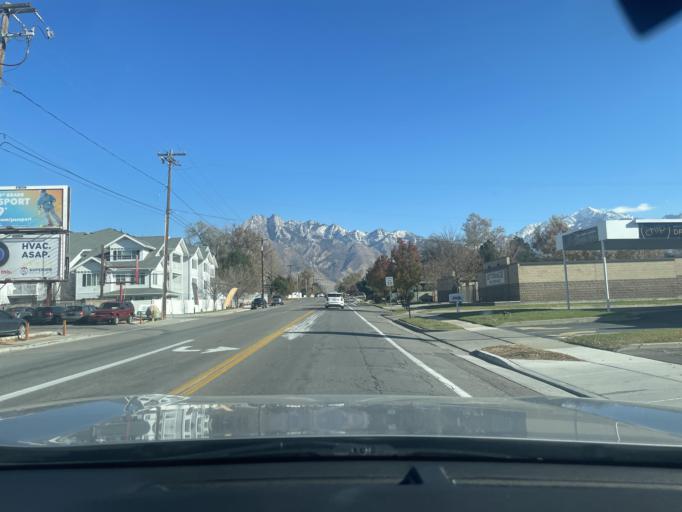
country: US
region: Utah
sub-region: Salt Lake County
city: Murray
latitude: 40.6496
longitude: -111.8655
